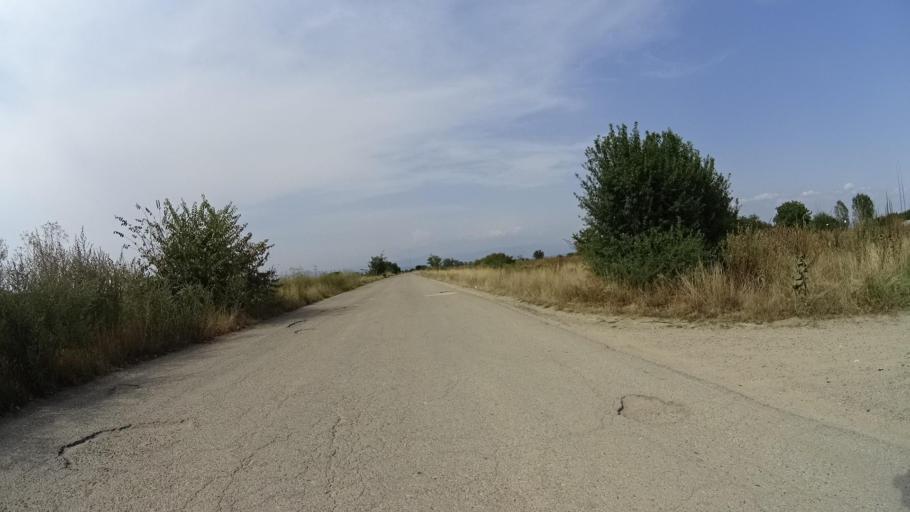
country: BG
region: Plovdiv
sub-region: Obshtina Kaloyanovo
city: Kaloyanovo
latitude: 42.3141
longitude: 24.7996
